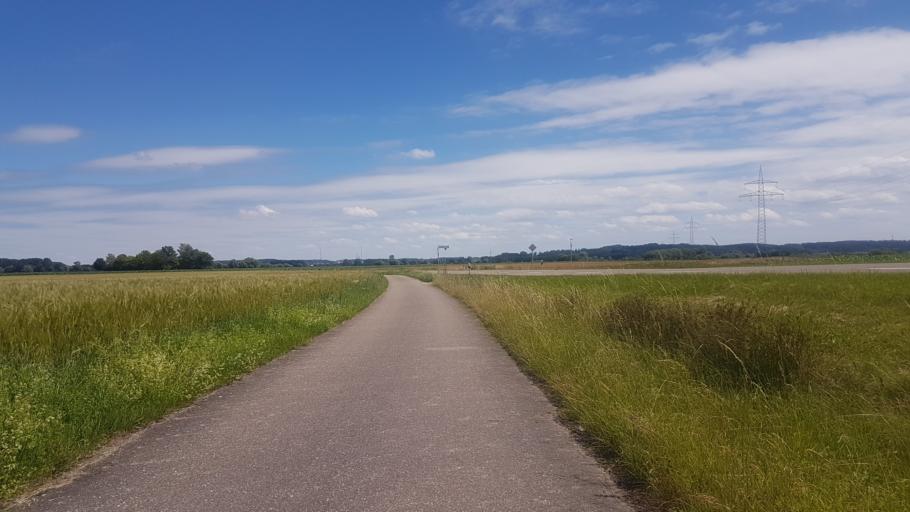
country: DE
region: Bavaria
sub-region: Swabia
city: Schwenningen
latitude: 48.6293
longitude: 10.6550
